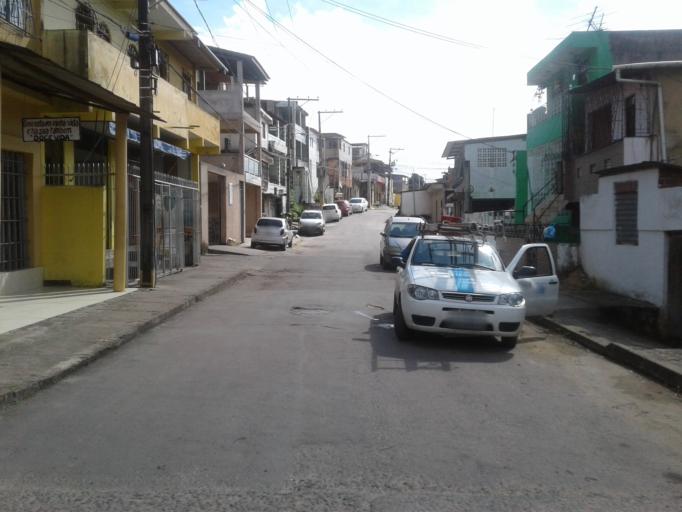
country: BR
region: Bahia
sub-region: Salvador
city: Salvador
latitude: -12.8832
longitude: -38.4755
